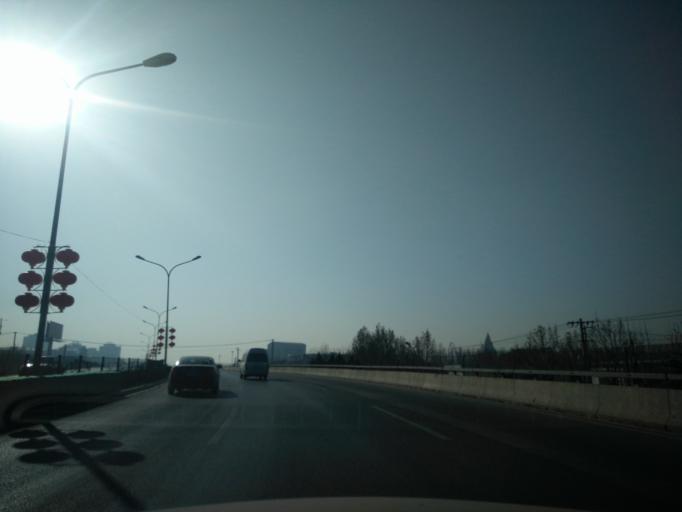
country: CN
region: Beijing
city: Dongfeng
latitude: 39.8715
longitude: 116.4941
